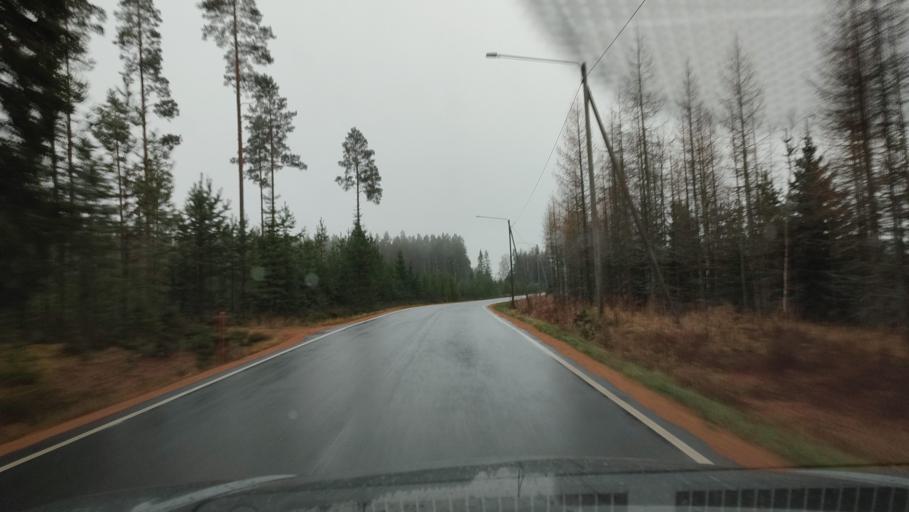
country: FI
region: Southern Ostrobothnia
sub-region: Suupohja
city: Karijoki
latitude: 62.1387
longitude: 21.6846
